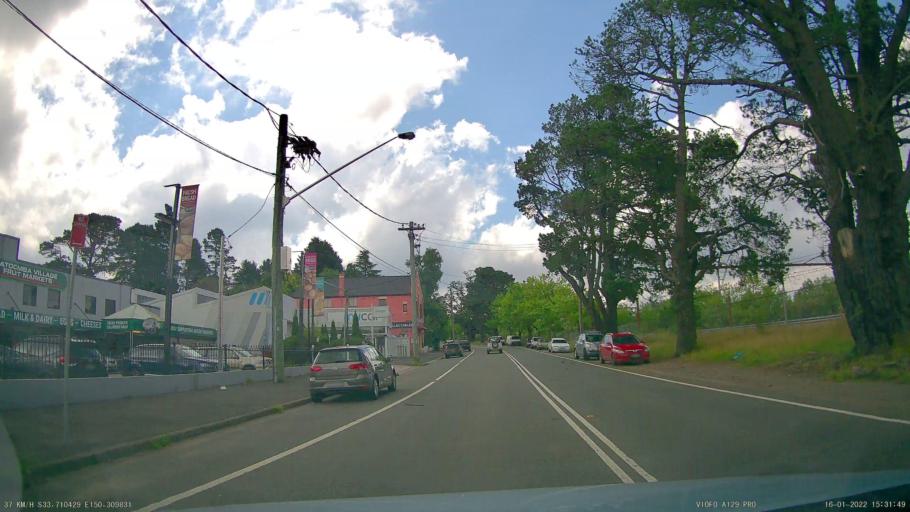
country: AU
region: New South Wales
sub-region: Blue Mountains Municipality
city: Katoomba
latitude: -33.7102
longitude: 150.3097
